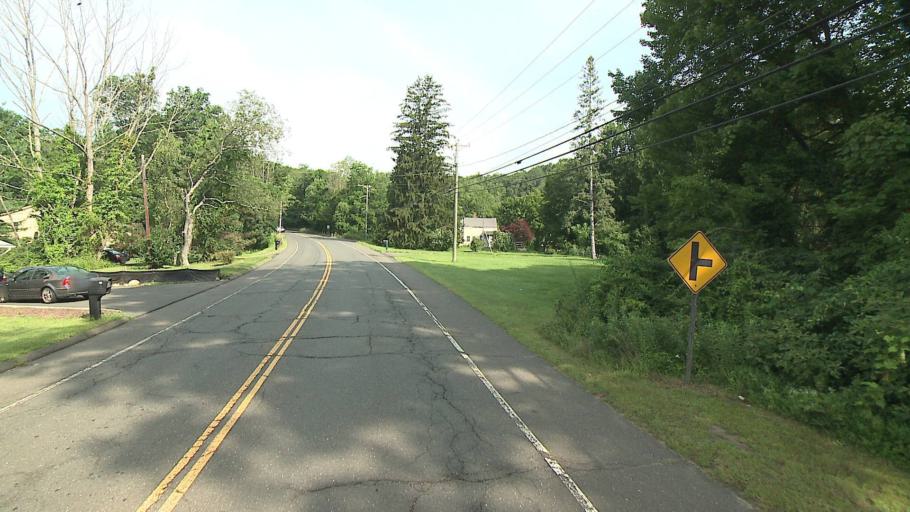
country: US
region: New York
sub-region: Putnam County
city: Putnam Lake
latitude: 41.4720
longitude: -73.4930
